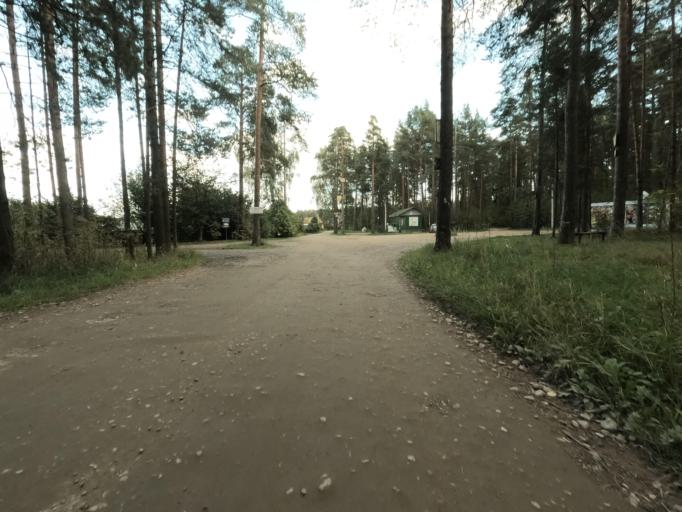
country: RU
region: Leningrad
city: Imeni Sverdlova
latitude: 59.8396
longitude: 30.7030
